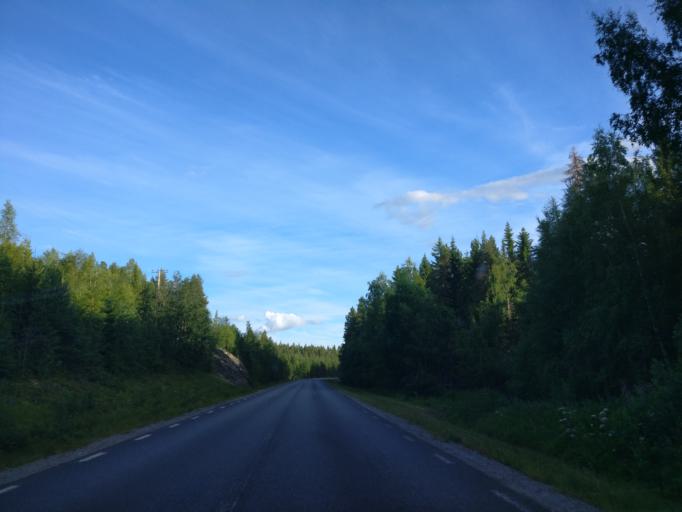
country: SE
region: Jaemtland
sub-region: Braecke Kommun
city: Braecke
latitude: 62.4146
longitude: 15.0145
